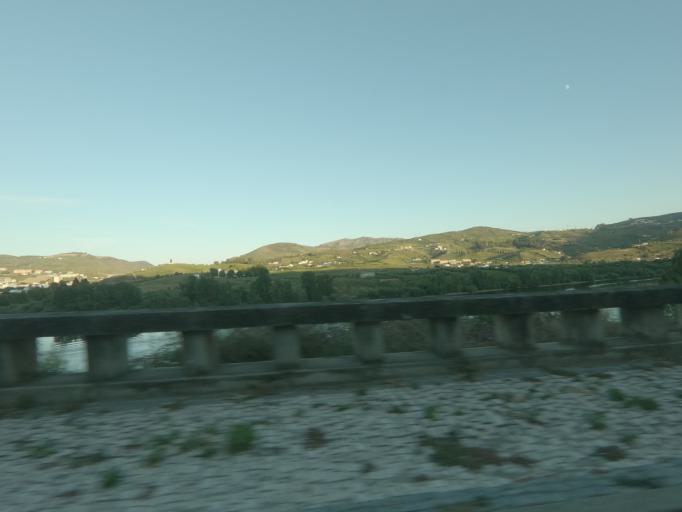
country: PT
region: Vila Real
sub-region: Peso da Regua
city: Godim
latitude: 41.1576
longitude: -7.8074
